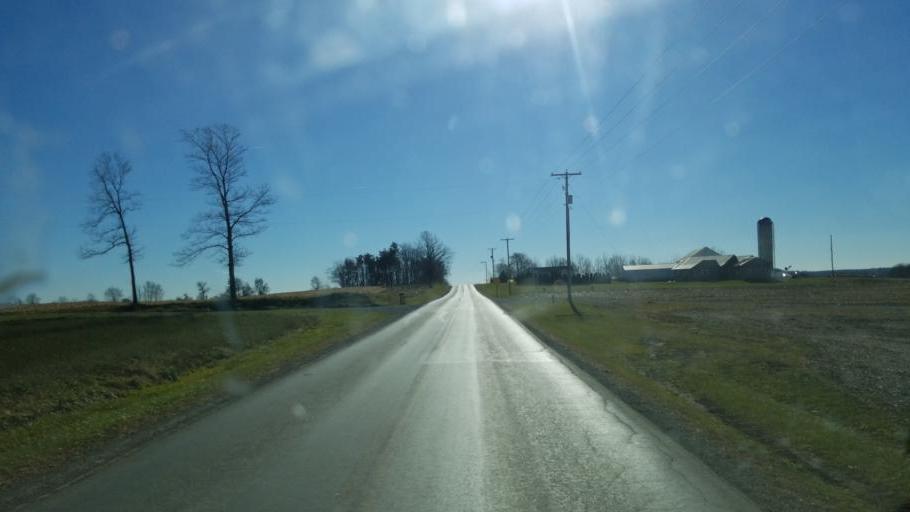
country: US
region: Ohio
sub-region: Huron County
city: Plymouth
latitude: 40.9488
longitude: -82.5838
